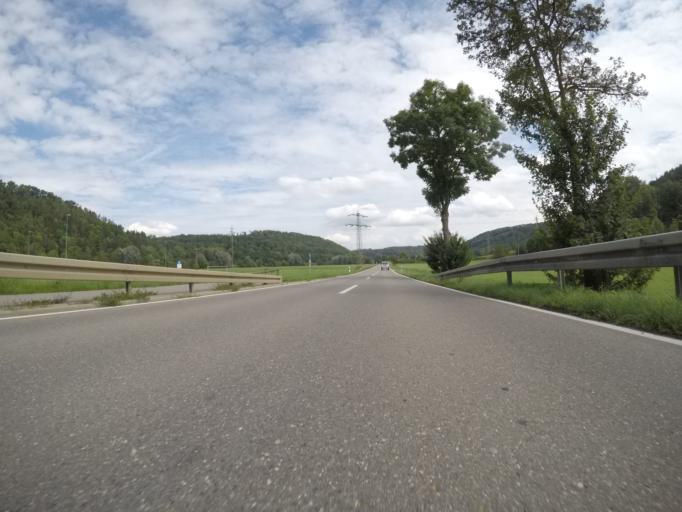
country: DE
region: Baden-Wuerttemberg
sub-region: Tuebingen Region
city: Hirrlingen
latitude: 48.4594
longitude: 8.8764
